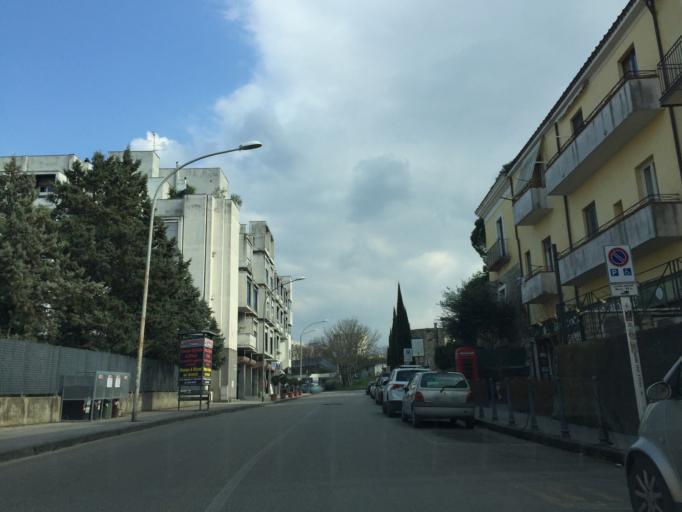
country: IT
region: Campania
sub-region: Provincia di Benevento
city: Benevento
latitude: 41.1323
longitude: 14.7816
